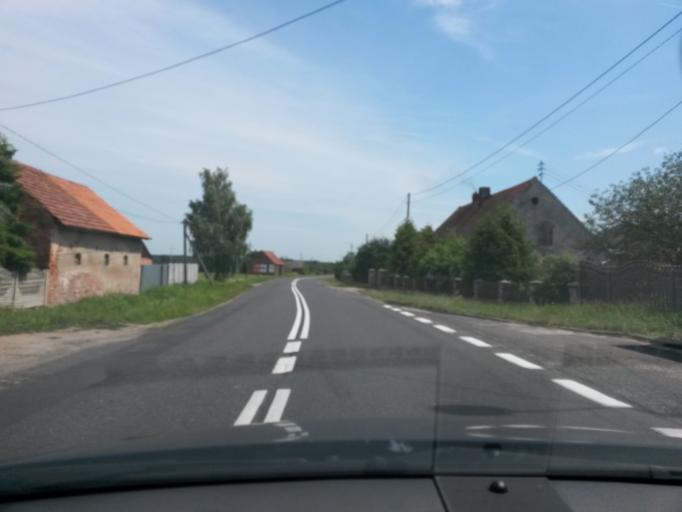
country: PL
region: Lower Silesian Voivodeship
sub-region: Powiat gorowski
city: Wasosz
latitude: 51.5896
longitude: 16.7523
